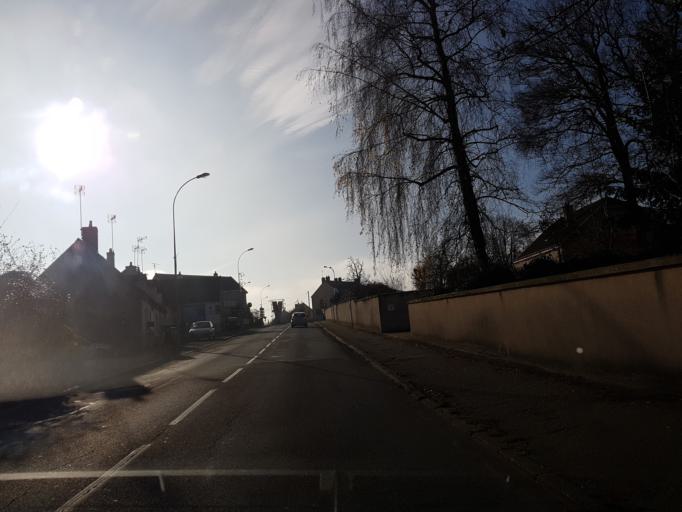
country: FR
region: Bourgogne
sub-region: Departement de Saone-et-Loire
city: Gueugnon
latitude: 46.6020
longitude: 4.0697
